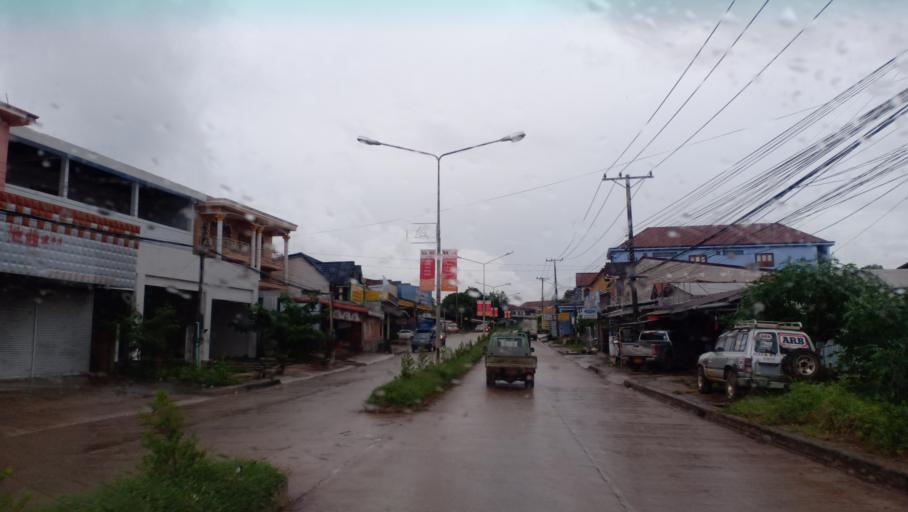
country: LA
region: Khammouan
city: Thakhek
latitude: 17.4039
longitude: 104.8254
